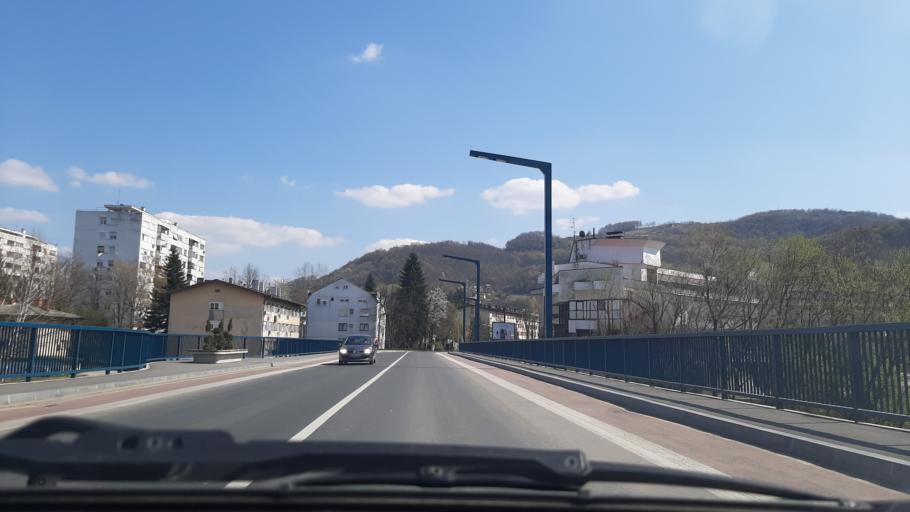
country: BA
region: Republika Srpska
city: Hiseti
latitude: 44.7608
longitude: 17.1828
